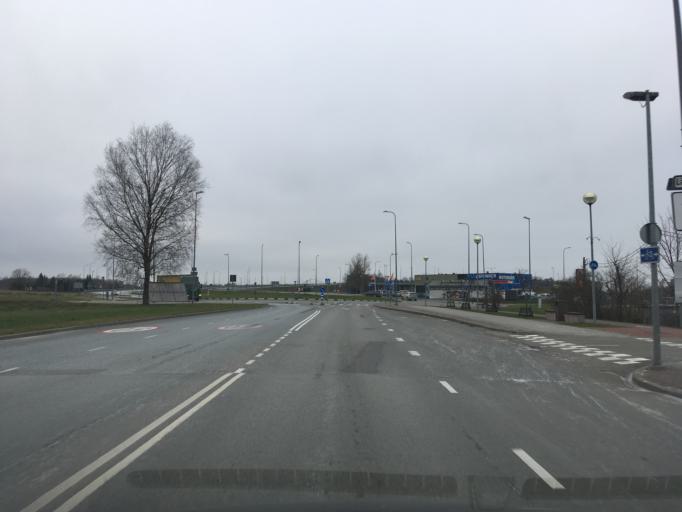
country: EE
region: Ida-Virumaa
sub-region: Johvi vald
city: Johvi
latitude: 59.3662
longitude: 27.3956
